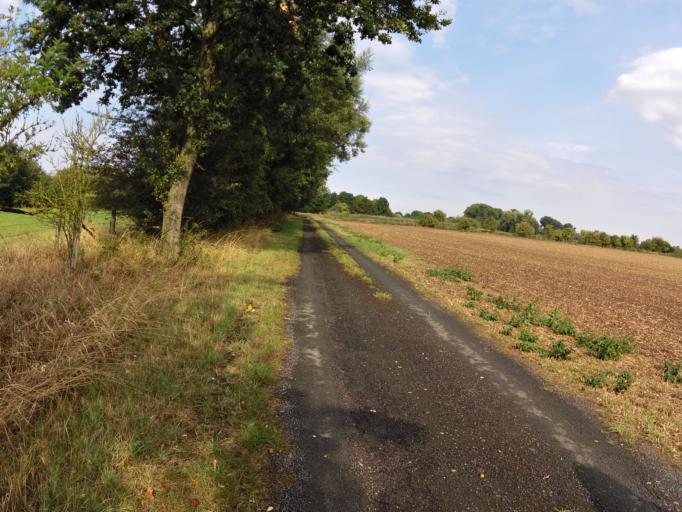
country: DE
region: Lower Saxony
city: Marklohe
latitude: 52.6600
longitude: 9.1853
